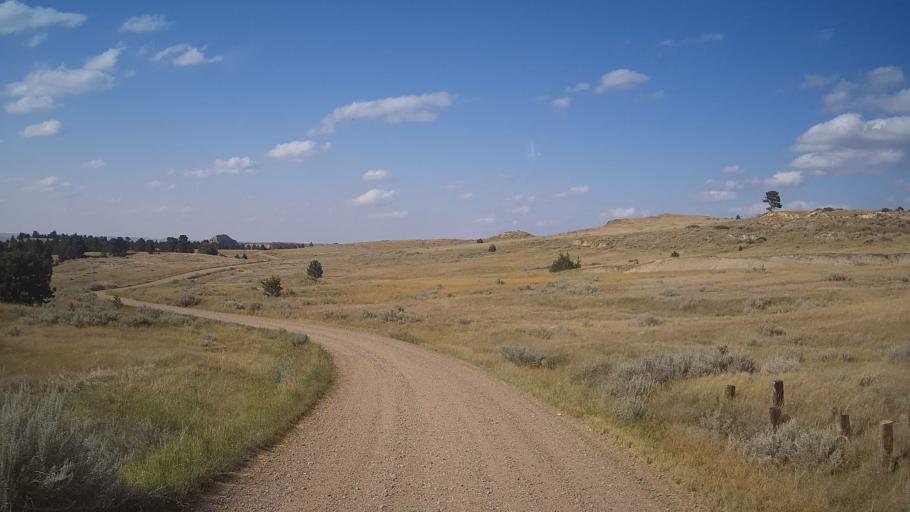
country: US
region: Montana
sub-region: Dawson County
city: Glendive
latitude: 47.0545
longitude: -104.6720
